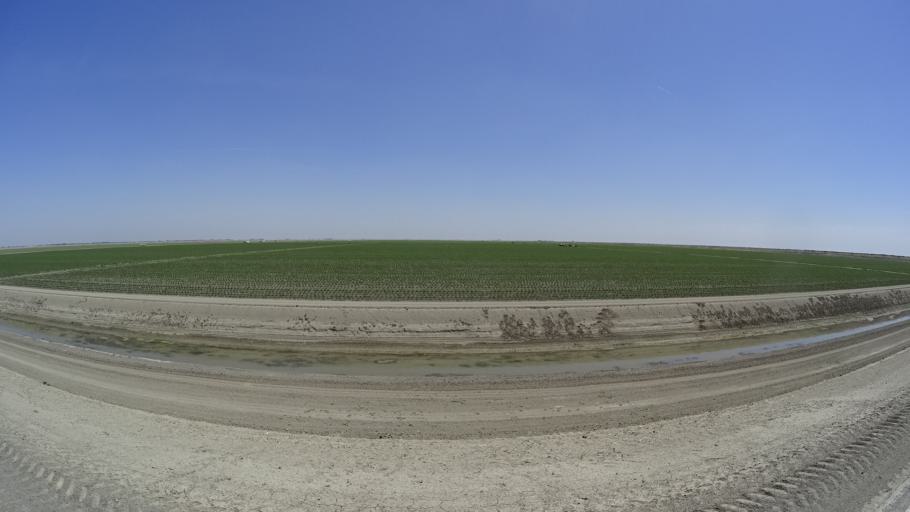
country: US
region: California
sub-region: Kings County
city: Corcoran
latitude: 36.0478
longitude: -119.6434
